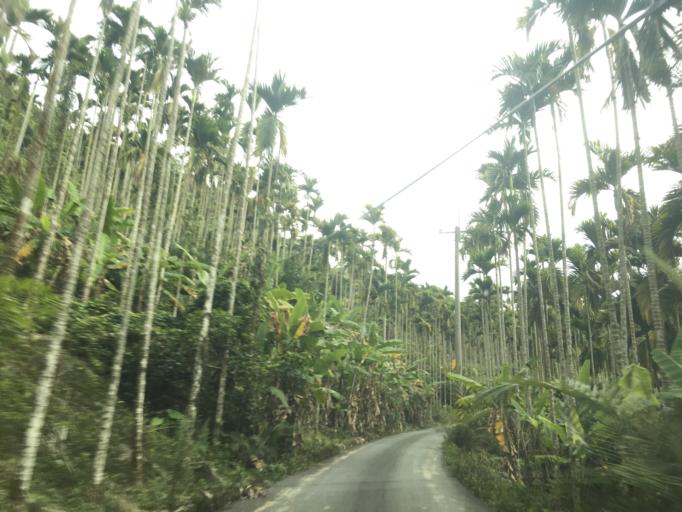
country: TW
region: Taiwan
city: Zhongxing New Village
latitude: 23.9757
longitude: 120.8214
